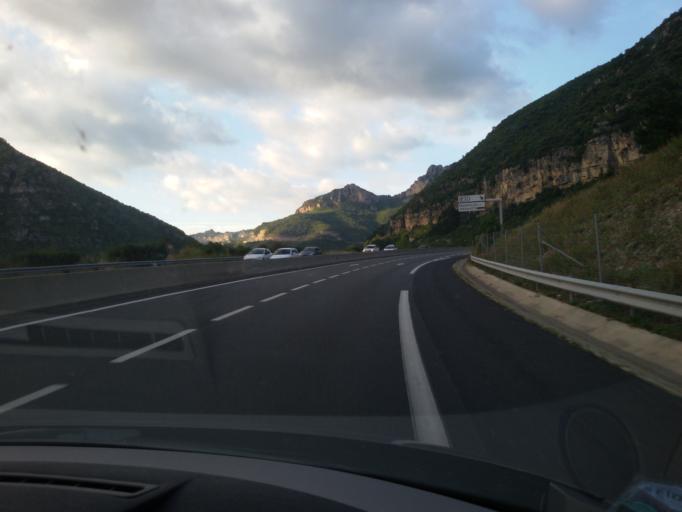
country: FR
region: Languedoc-Roussillon
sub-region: Departement de l'Herault
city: Lodeve
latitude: 43.7922
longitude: 3.3261
